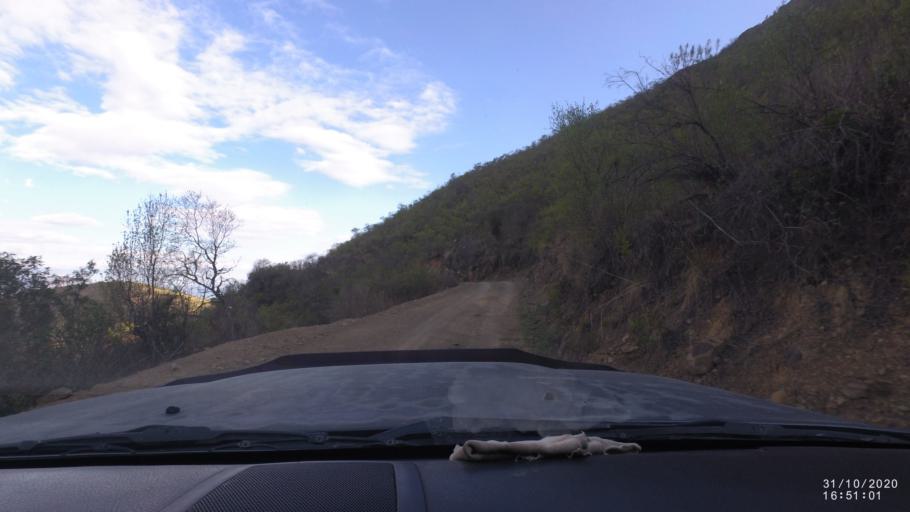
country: BO
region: Chuquisaca
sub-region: Provincia Zudanez
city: Mojocoya
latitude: -18.5106
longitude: -64.5723
